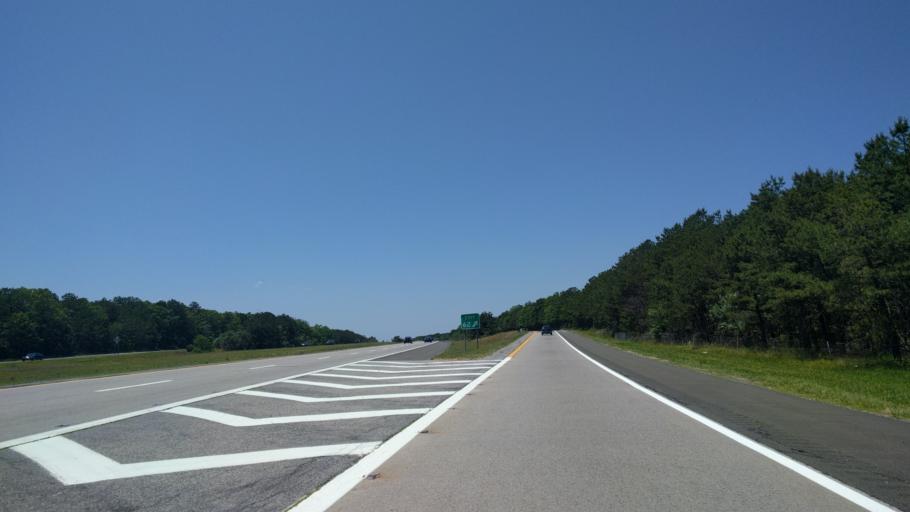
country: US
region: New York
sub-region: Suffolk County
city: Eastport
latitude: 40.8481
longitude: -72.7149
